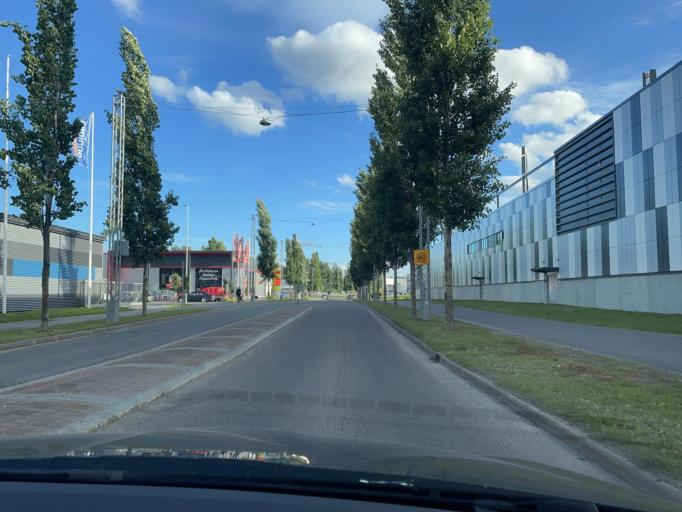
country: FI
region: Central Finland
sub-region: Jyvaeskylae
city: Jyvaeskylae
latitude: 62.2564
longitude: 25.7774
